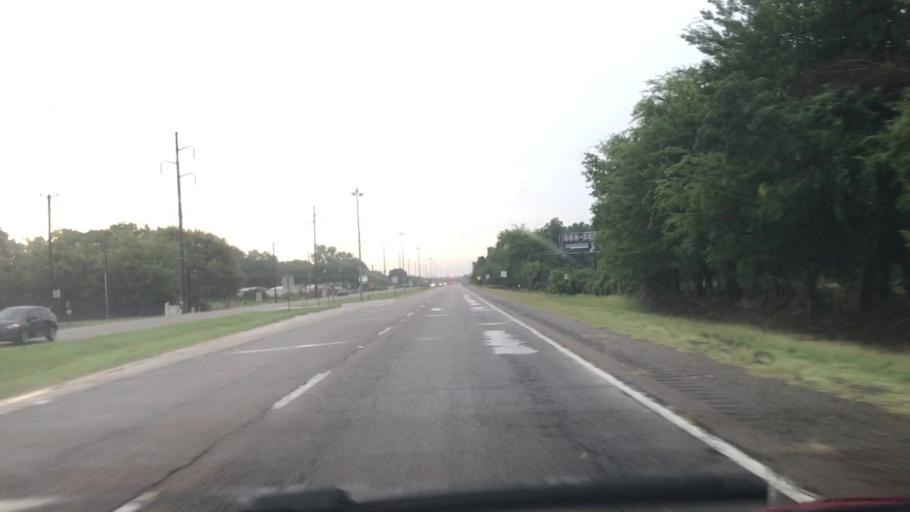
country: US
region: Louisiana
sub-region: Bossier Parish
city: Red Chute
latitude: 32.5386
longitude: -93.6562
